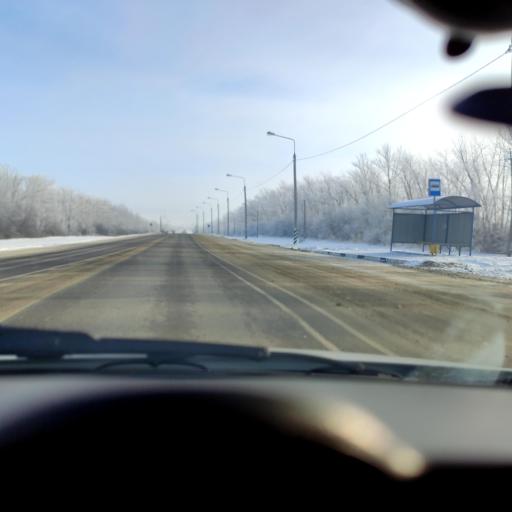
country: RU
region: Kursk
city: Kshenskiy
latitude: 51.6212
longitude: 37.6074
